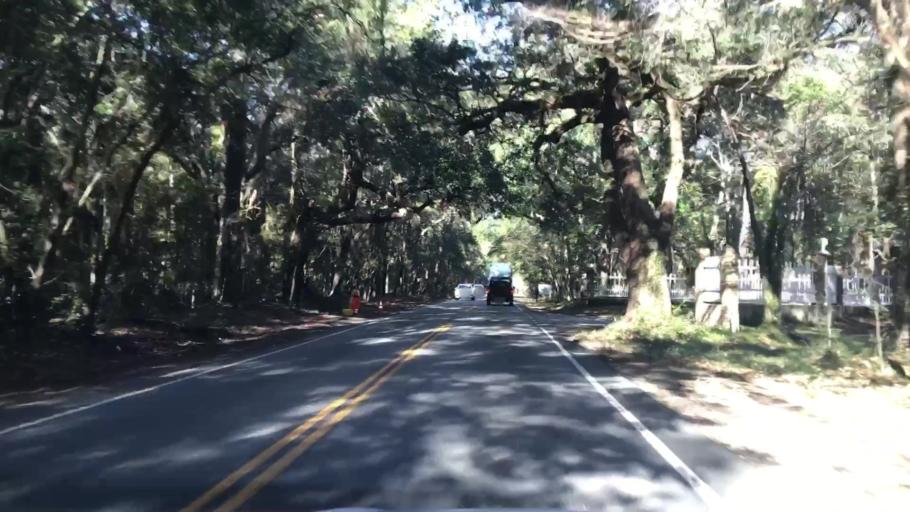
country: US
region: South Carolina
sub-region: Charleston County
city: Shell Point
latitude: 32.8643
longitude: -80.0825
